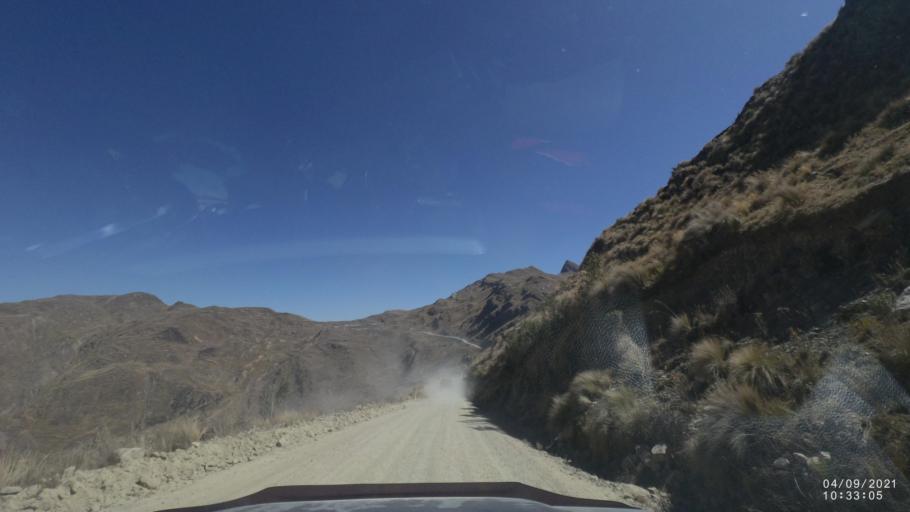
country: BO
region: Cochabamba
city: Sipe Sipe
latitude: -17.2972
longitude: -66.4469
